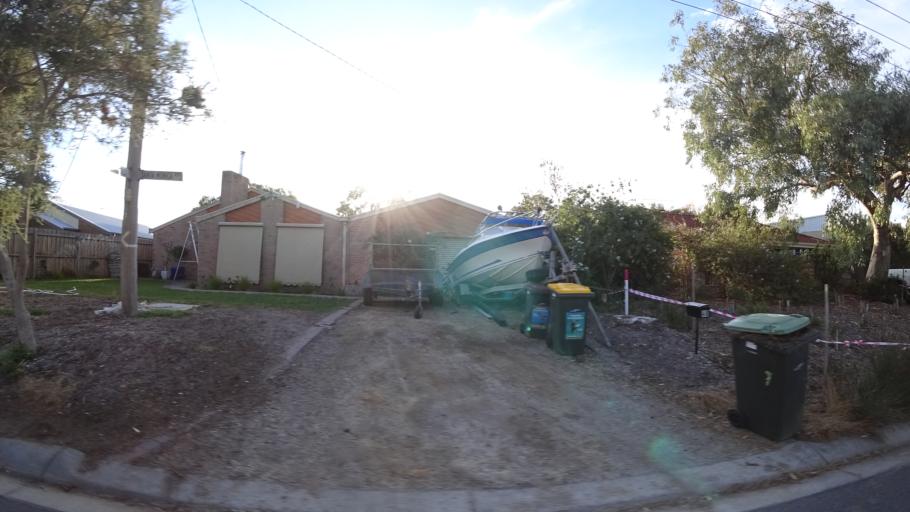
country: AU
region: Victoria
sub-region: Queenscliffe
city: Queenscliff
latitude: -38.2743
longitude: 144.6081
